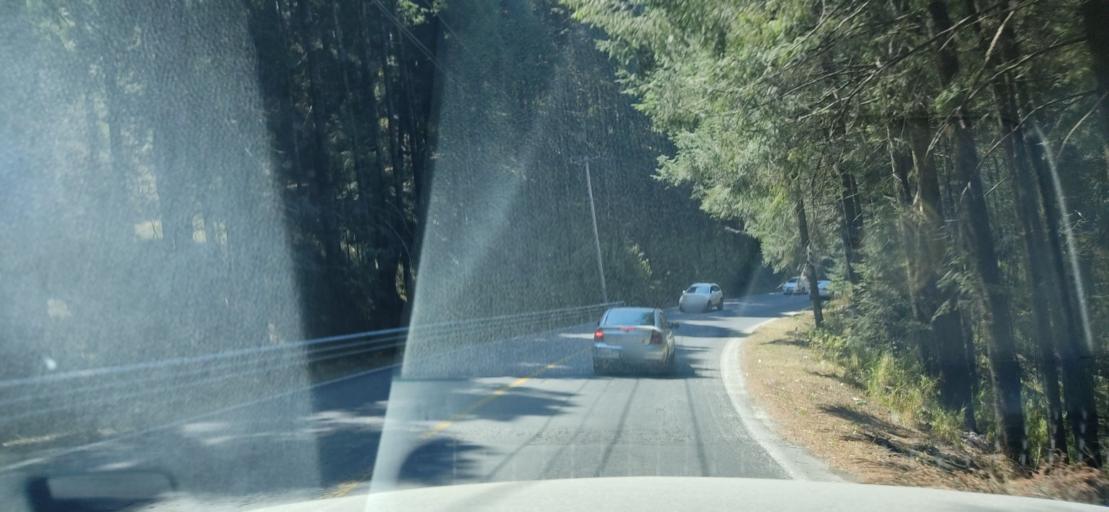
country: MX
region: Mexico
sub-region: Ocoyoacac
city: San Jeronimo Acazulco
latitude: 19.2613
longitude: -99.3718
